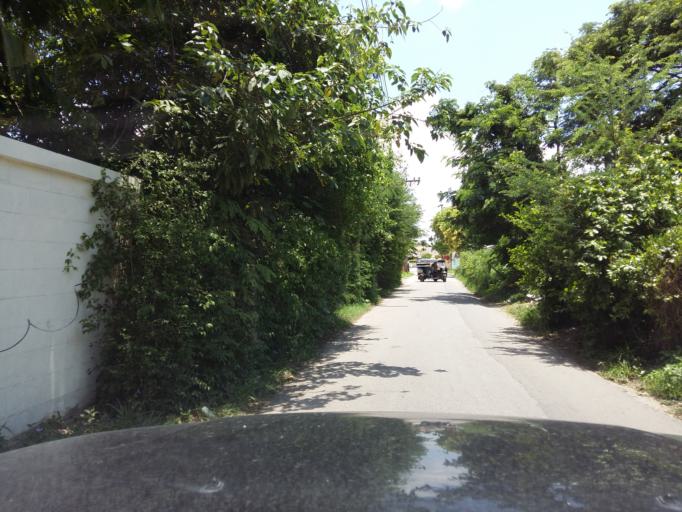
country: TH
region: Chiang Mai
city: Chiang Mai
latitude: 18.7688
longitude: 99.0122
